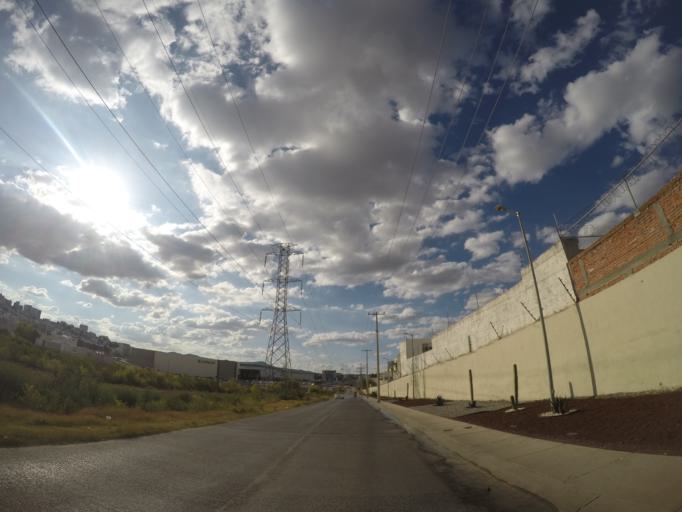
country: MX
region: San Luis Potosi
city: Escalerillas
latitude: 22.1249
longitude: -101.0263
